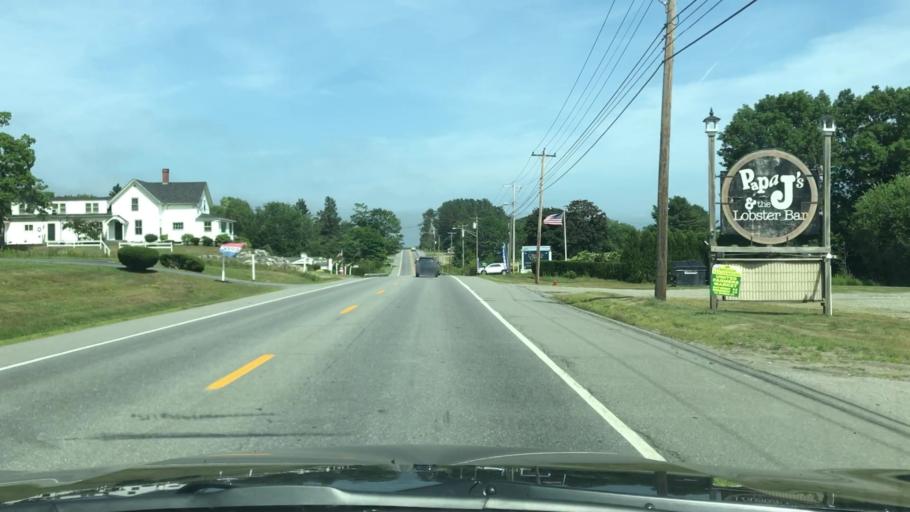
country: US
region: Maine
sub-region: Waldo County
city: Belfast
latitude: 44.4299
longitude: -68.9714
